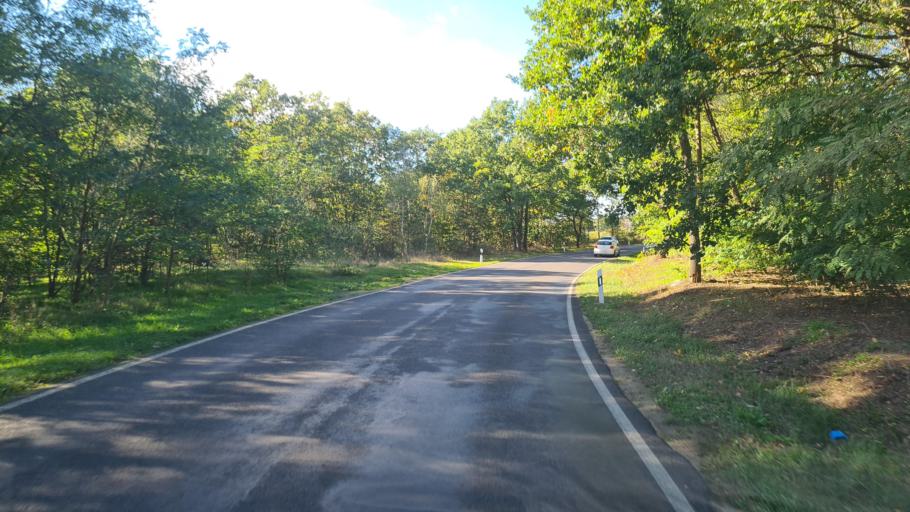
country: DE
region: Brandenburg
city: Kolkwitz
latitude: 51.7636
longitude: 14.2687
